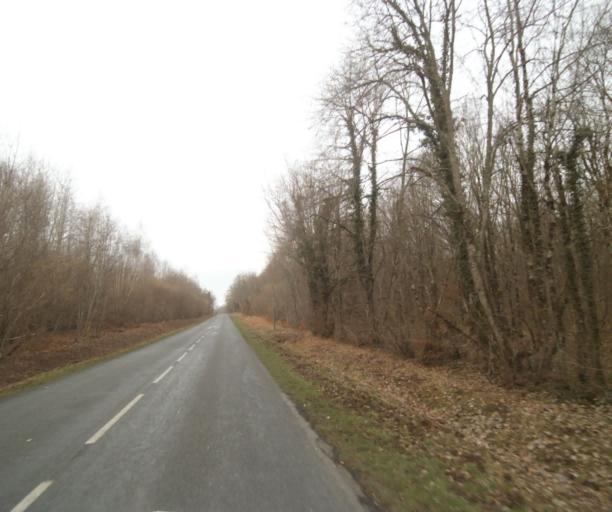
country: FR
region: Champagne-Ardenne
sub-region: Departement de la Haute-Marne
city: Villiers-en-Lieu
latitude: 48.7042
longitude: 4.8932
